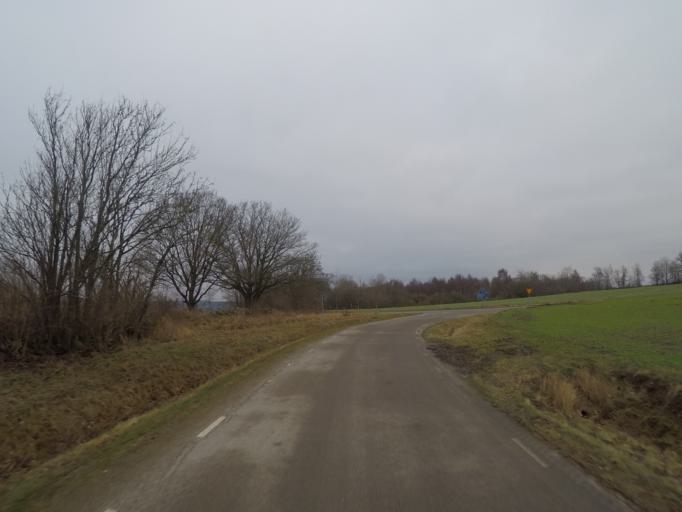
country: SE
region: Skane
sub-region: Hoors Kommun
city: Loberod
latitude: 55.7927
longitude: 13.4035
